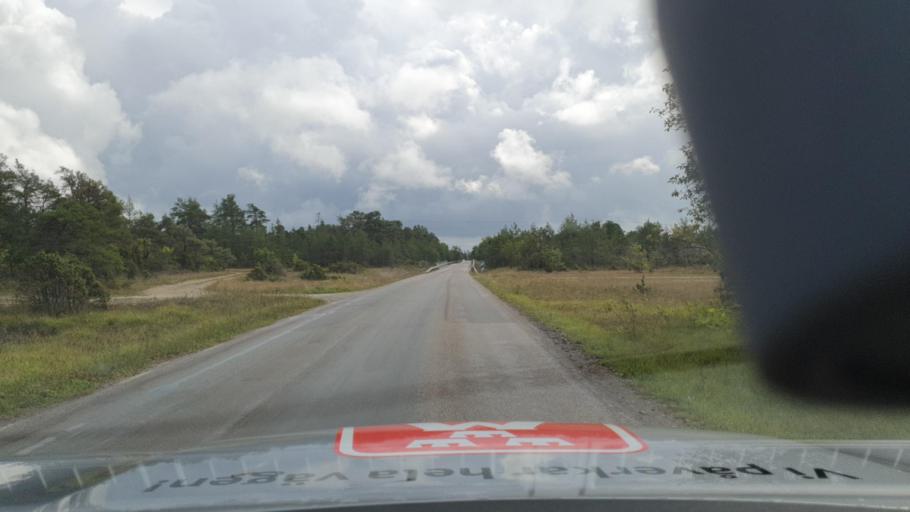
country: SE
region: Gotland
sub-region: Gotland
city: Slite
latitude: 57.7241
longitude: 18.7503
